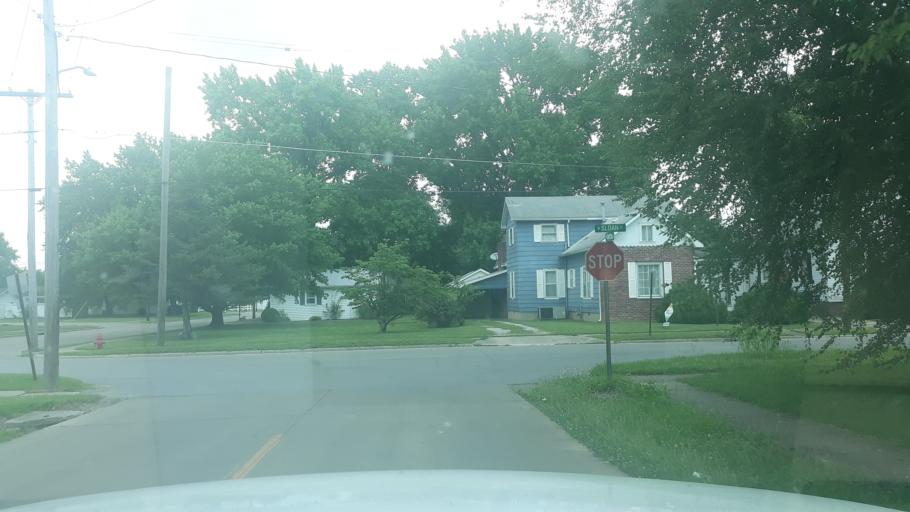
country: US
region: Illinois
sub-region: Saline County
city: Harrisburg
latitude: 37.7312
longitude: -88.5527
